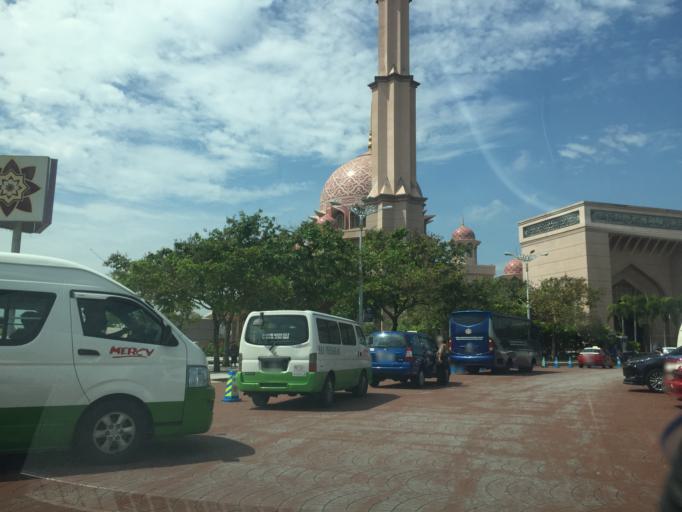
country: MY
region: Putrajaya
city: Putrajaya
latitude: 2.9348
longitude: 101.6905
